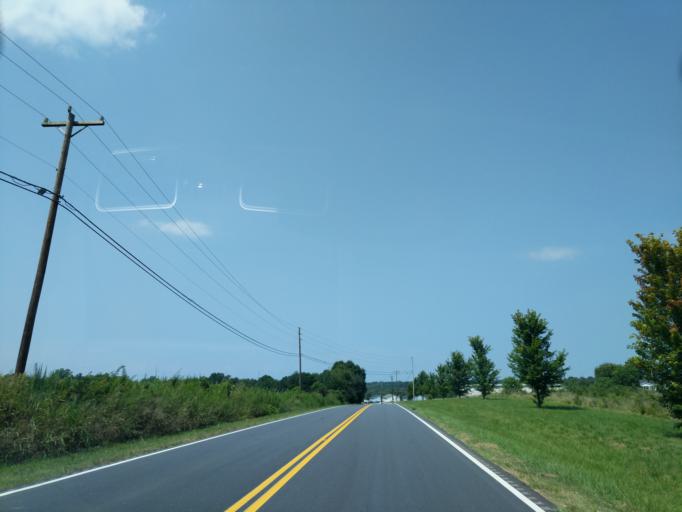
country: US
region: South Carolina
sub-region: Spartanburg County
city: Duncan
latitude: 34.9172
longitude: -82.1445
